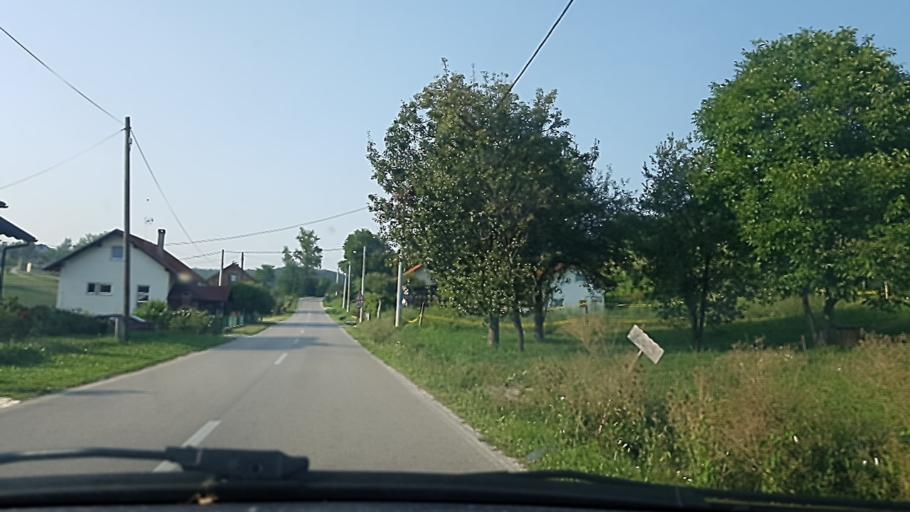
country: HR
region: Zagrebacka
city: Jakovlje
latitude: 45.9715
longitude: 15.8324
